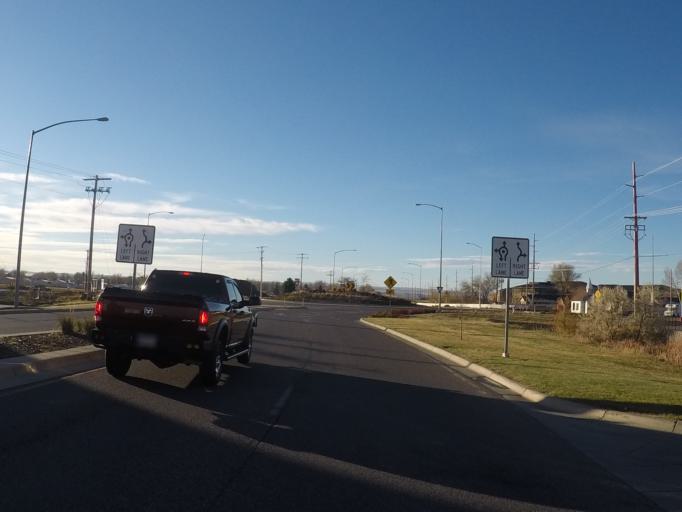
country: US
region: Montana
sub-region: Yellowstone County
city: Billings
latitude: 45.7705
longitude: -108.6177
